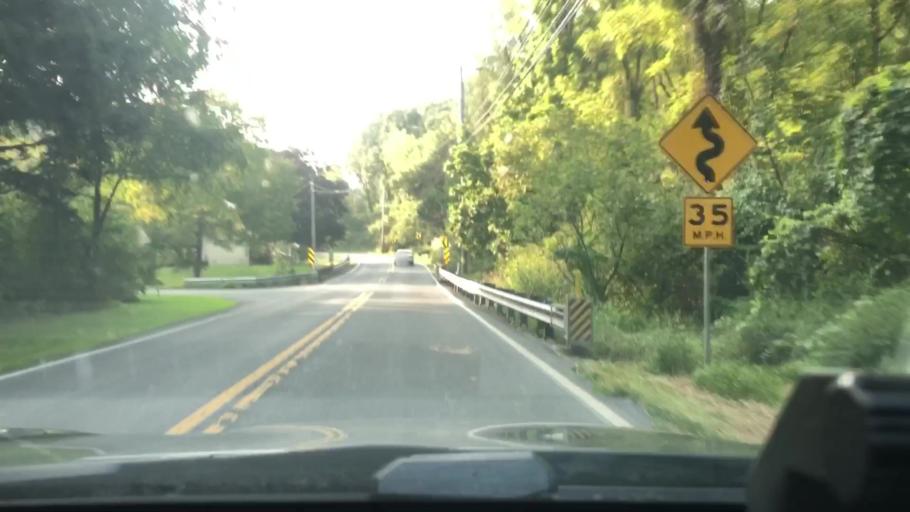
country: US
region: Pennsylvania
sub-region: Berks County
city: Kutztown
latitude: 40.5525
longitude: -75.8031
